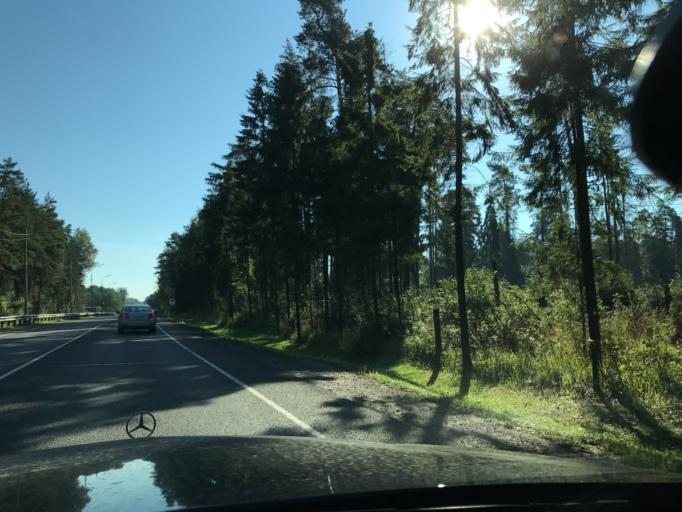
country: RU
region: Moskovskaya
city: Losino-Petrovskiy
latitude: 55.9582
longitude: 38.2499
